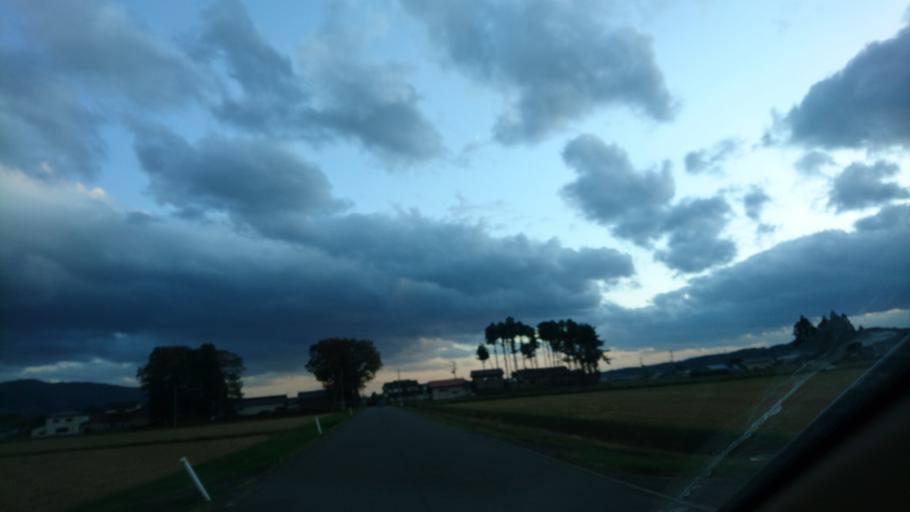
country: JP
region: Iwate
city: Mizusawa
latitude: 39.0741
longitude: 141.1415
